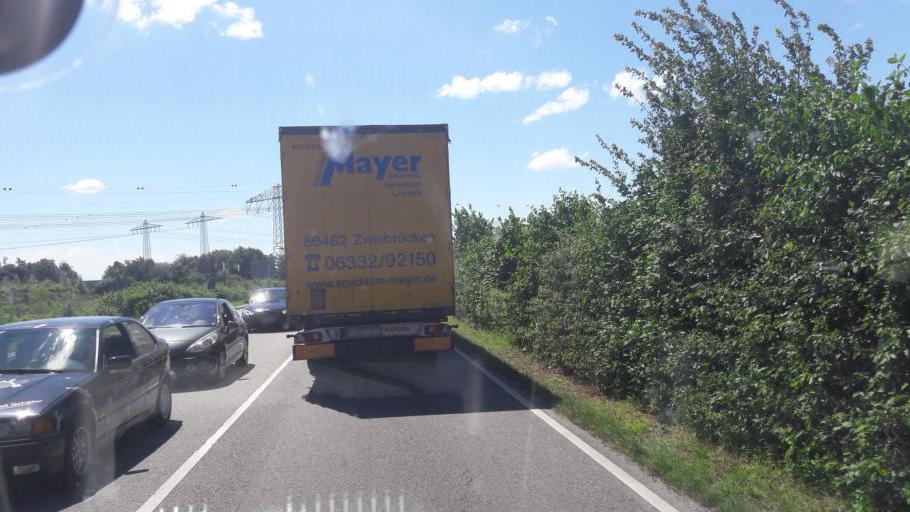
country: DE
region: Baden-Wuerttemberg
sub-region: Karlsruhe Region
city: Forst
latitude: 49.1328
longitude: 8.5712
